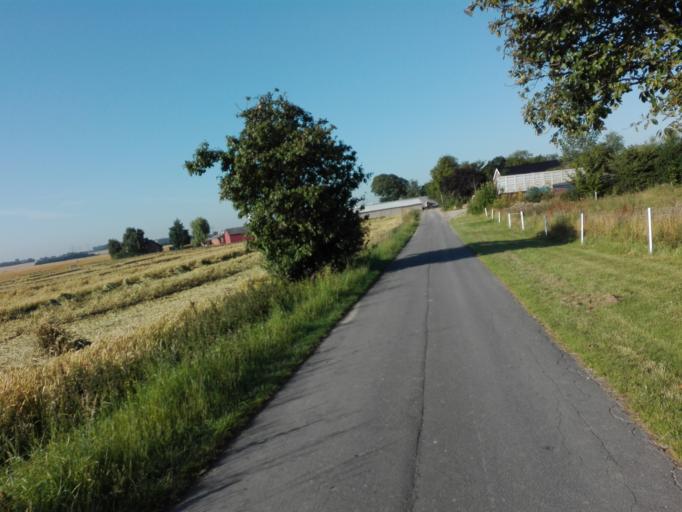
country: DK
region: Central Jutland
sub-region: Arhus Kommune
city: Marslet
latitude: 56.0789
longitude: 10.1457
